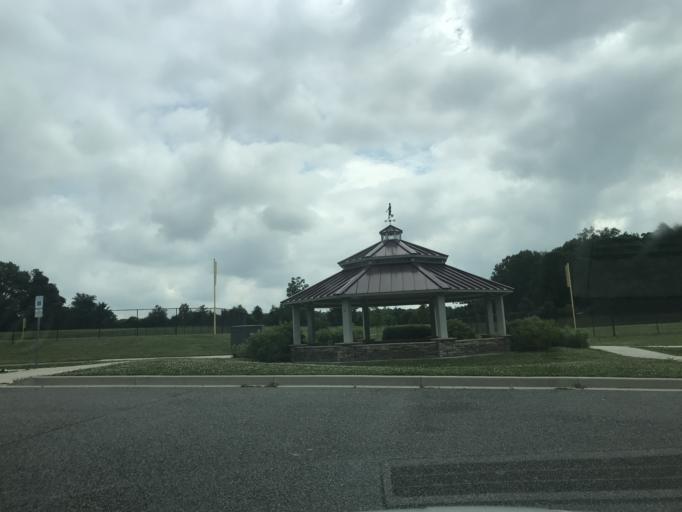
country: US
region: Maryland
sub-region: Harford County
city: Bel Air South
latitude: 39.5486
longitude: -76.2813
